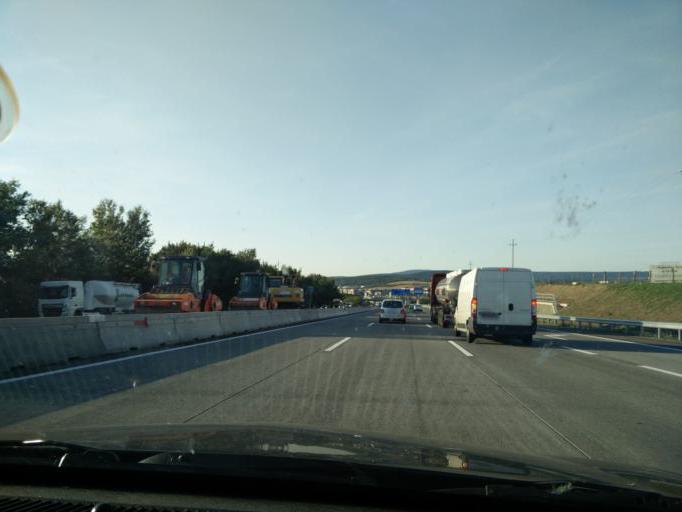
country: HU
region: Pest
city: Toeroekbalint
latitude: 47.4401
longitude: 18.8918
